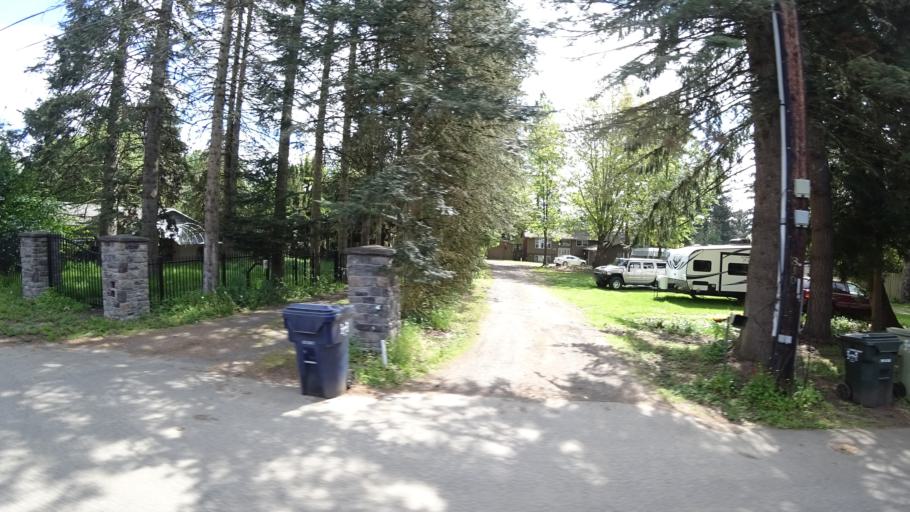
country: US
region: Oregon
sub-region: Washington County
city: Aloha
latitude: 45.5140
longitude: -122.8941
